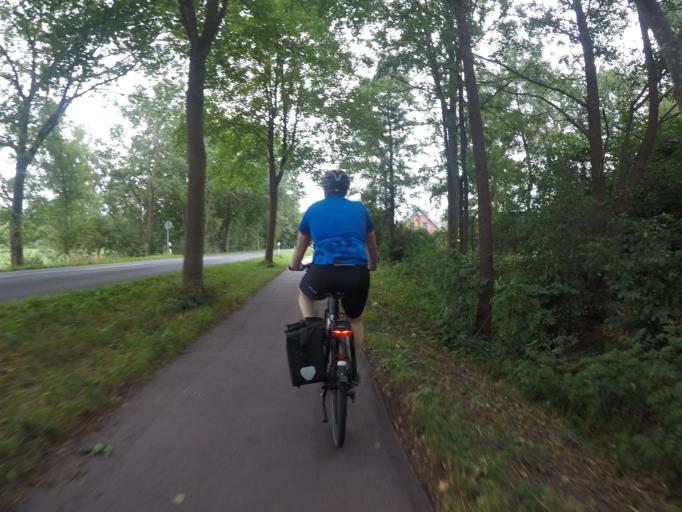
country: DE
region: Lower Saxony
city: Himmelpforten
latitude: 53.6363
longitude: 9.2983
